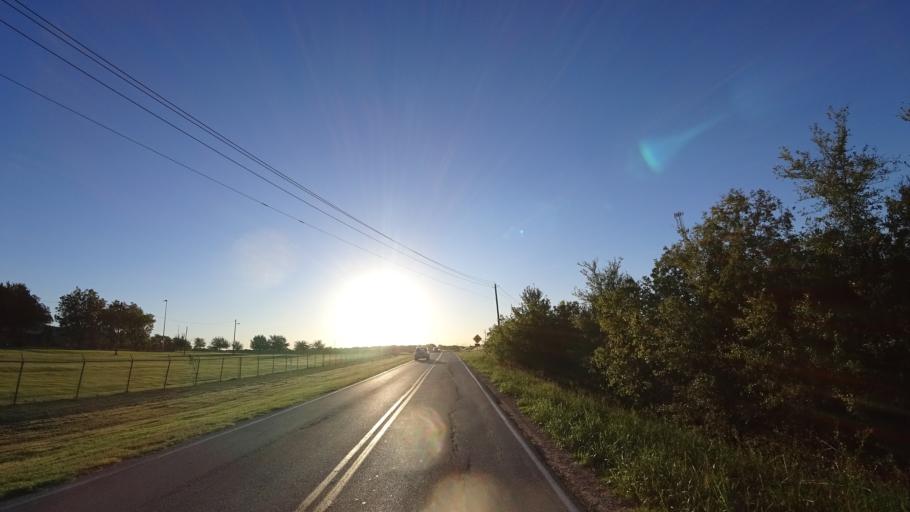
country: US
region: Texas
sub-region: Travis County
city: Hornsby Bend
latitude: 30.2856
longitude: -97.6194
